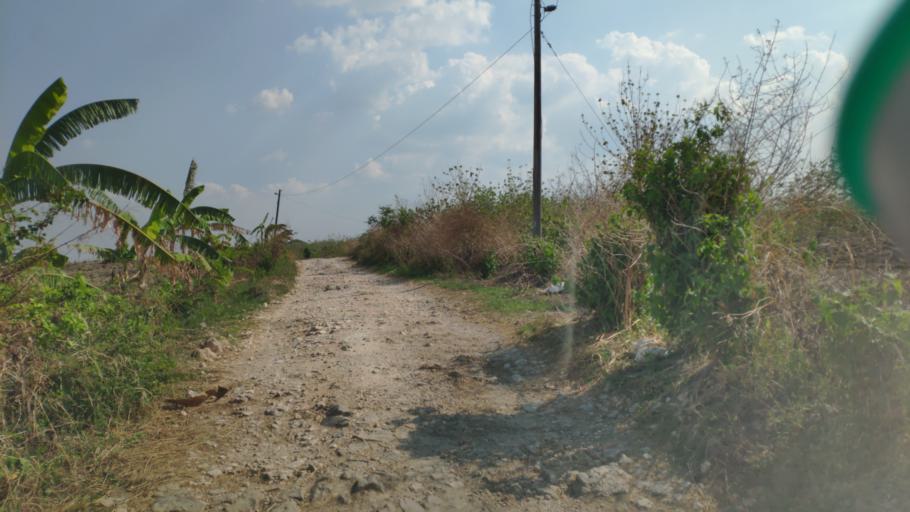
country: ID
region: Central Java
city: Randublatung
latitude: -7.2186
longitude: 111.3509
